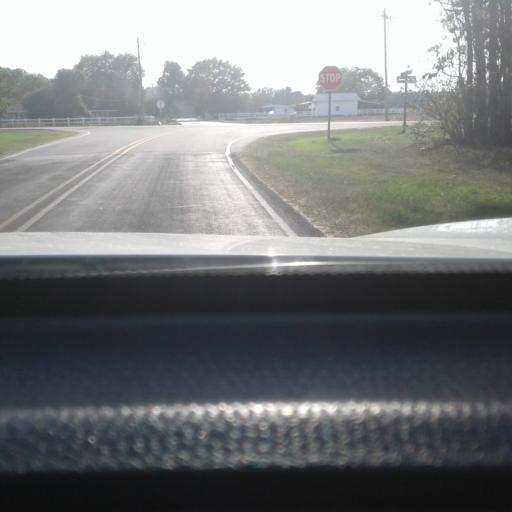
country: US
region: North Carolina
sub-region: Harnett County
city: Dunn
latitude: 35.3355
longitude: -78.5895
